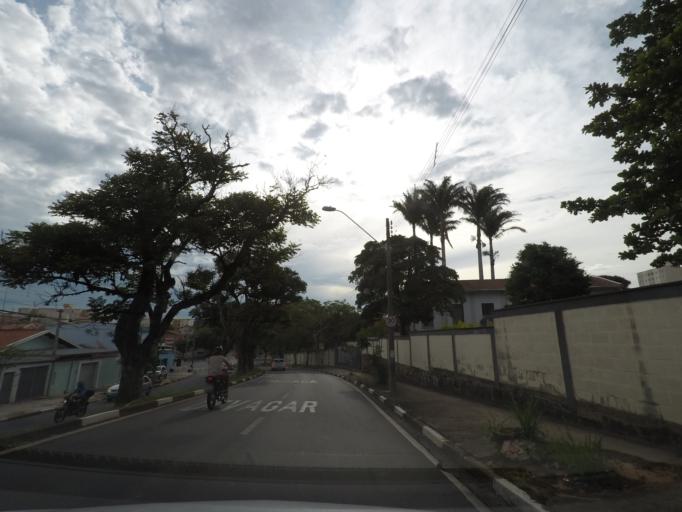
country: BR
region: Sao Paulo
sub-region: Campinas
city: Campinas
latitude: -22.8996
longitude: -47.1006
